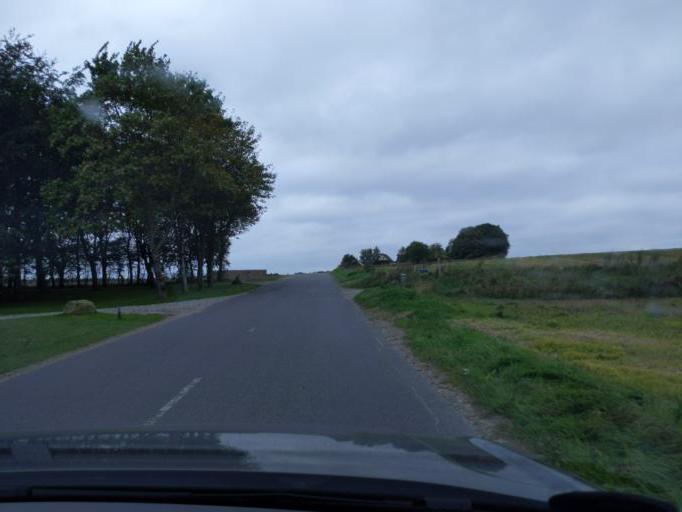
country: DK
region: Central Jutland
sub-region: Viborg Kommune
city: Bjerringbro
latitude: 56.5347
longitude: 9.5957
